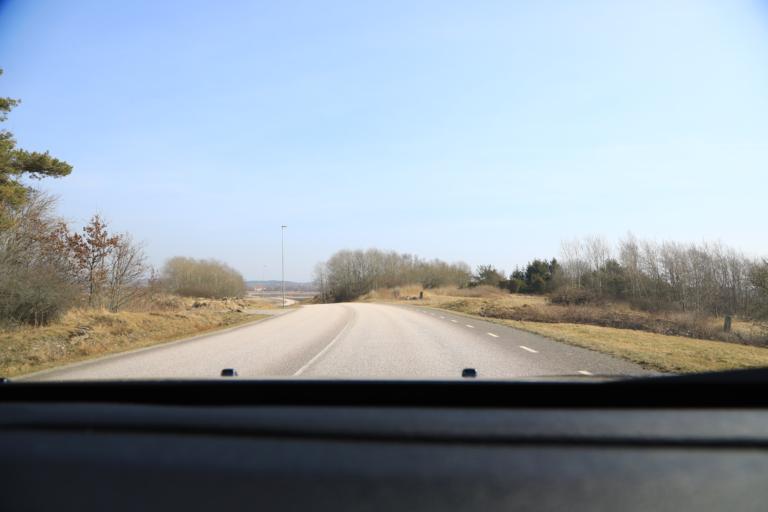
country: SE
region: Halland
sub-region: Kungsbacka Kommun
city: Frillesas
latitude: 57.2538
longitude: 12.1600
